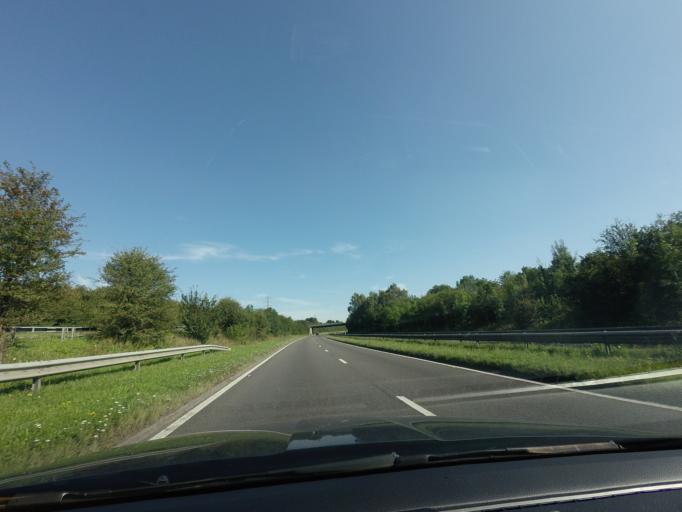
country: GB
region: England
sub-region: Derbyshire
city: Chesterfield
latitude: 53.2096
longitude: -1.3810
